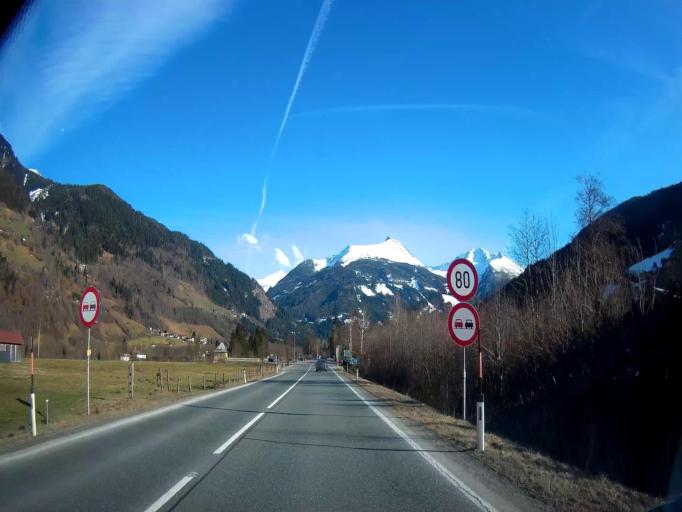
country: AT
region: Salzburg
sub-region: Politischer Bezirk Sankt Johann im Pongau
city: Bad Gastein
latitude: 47.1447
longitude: 13.1192
